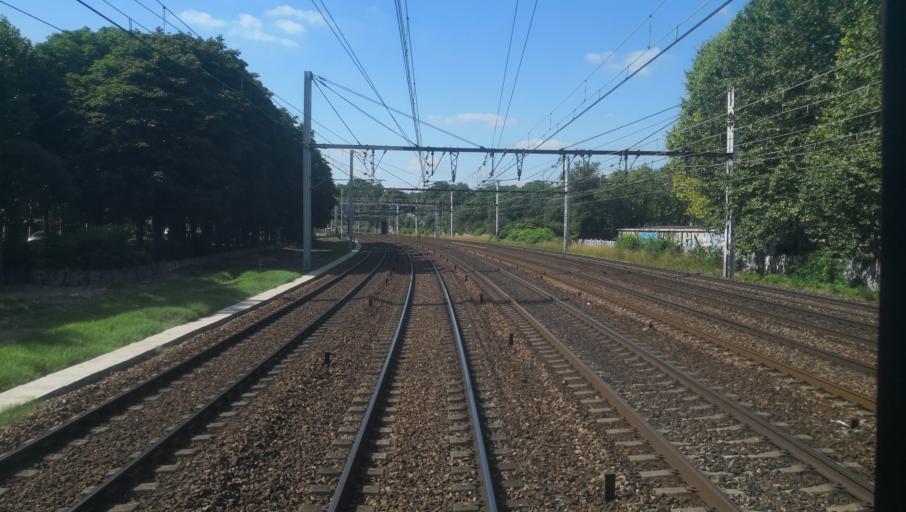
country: FR
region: Ile-de-France
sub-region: Departement du Val-de-Marne
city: Alfortville
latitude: 48.8076
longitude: 2.4240
